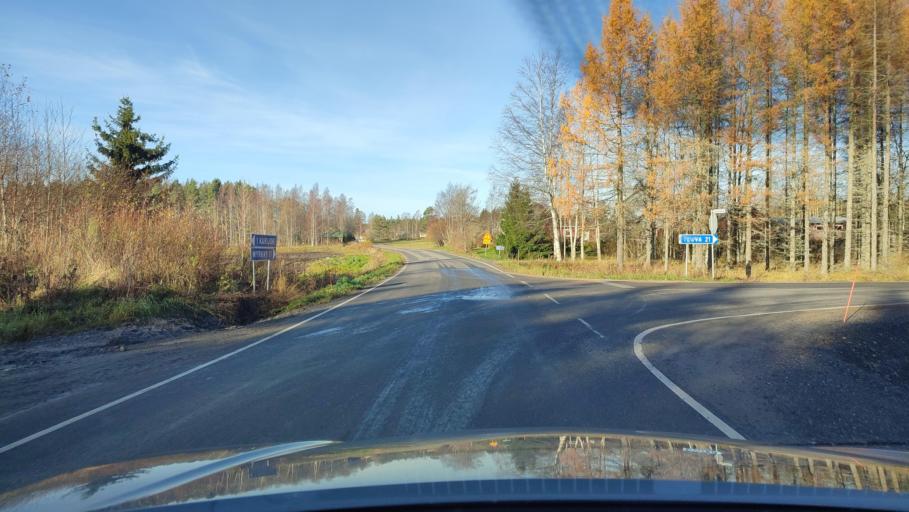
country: FI
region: Southern Ostrobothnia
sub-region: Suupohja
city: Karijoki
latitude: 62.3132
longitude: 21.7018
